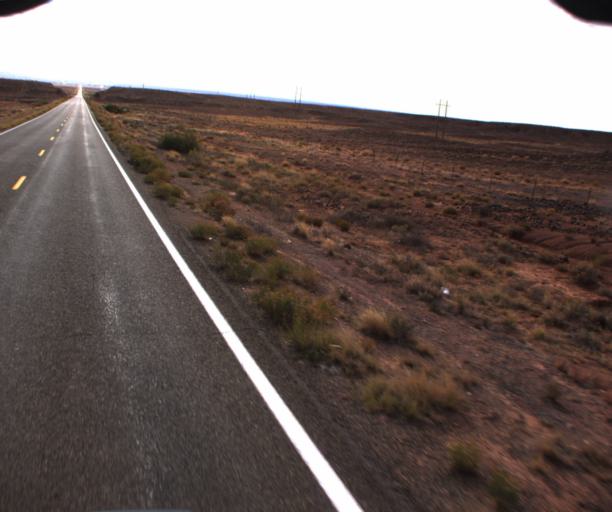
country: US
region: Arizona
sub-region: Apache County
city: Many Farms
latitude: 36.5418
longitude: -109.5248
